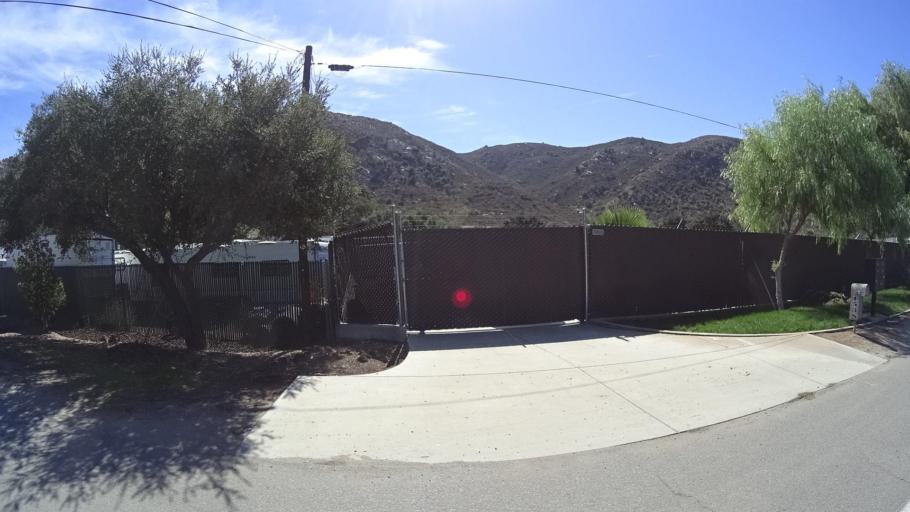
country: US
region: California
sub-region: San Diego County
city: Harbison Canyon
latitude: 32.8558
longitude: -116.8418
